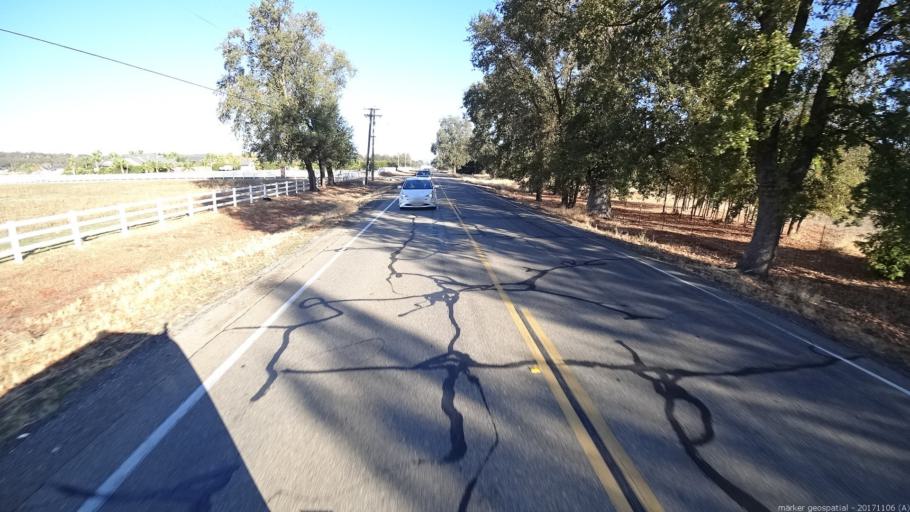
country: US
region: California
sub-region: Shasta County
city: Palo Cedro
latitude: 40.5271
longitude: -122.2385
